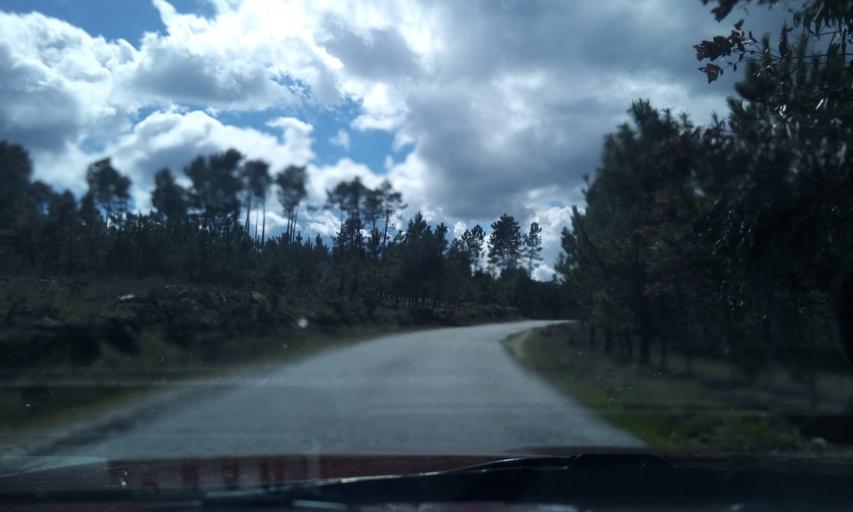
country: PT
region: Guarda
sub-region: Fornos de Algodres
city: Fornos de Algodres
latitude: 40.6559
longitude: -7.5105
